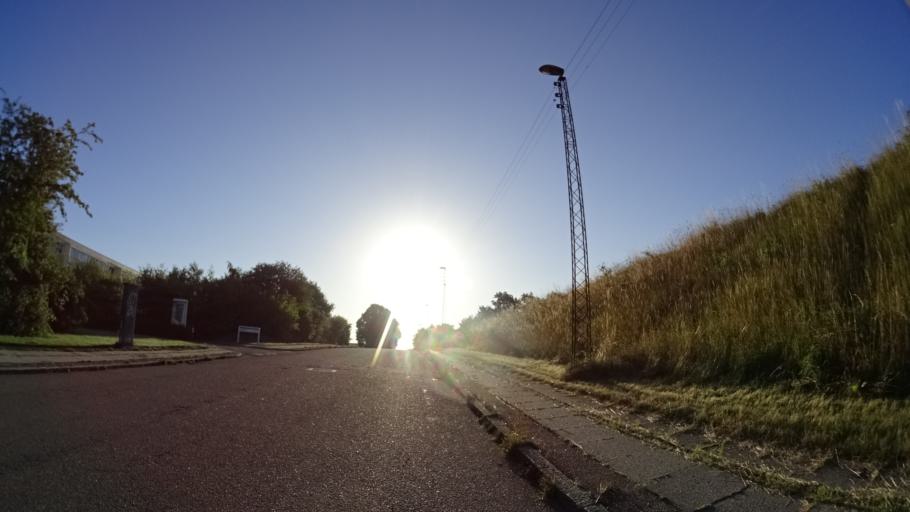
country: DK
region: Central Jutland
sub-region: Arhus Kommune
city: Arhus
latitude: 56.1279
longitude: 10.1743
